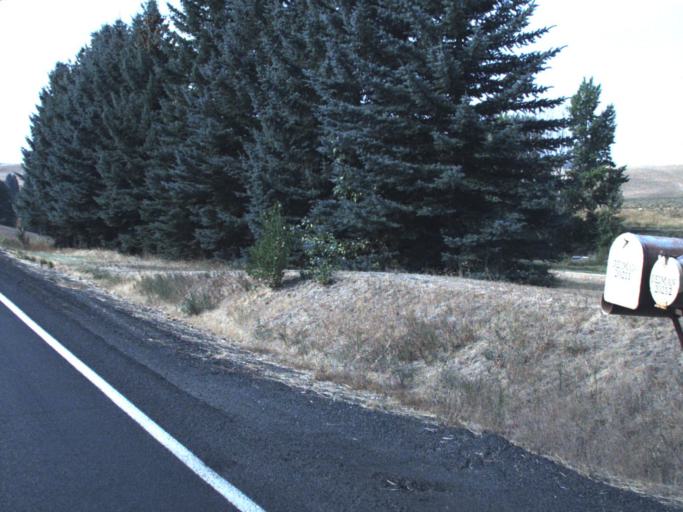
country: US
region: Washington
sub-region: Whitman County
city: Pullman
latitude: 46.9417
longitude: -117.0994
